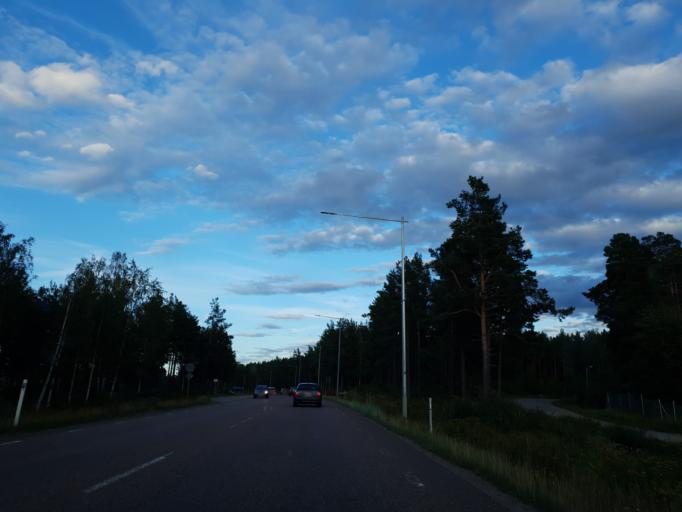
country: SE
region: Gaevleborg
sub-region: Soderhamns Kommun
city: Soderhamn
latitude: 61.2920
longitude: 17.0445
